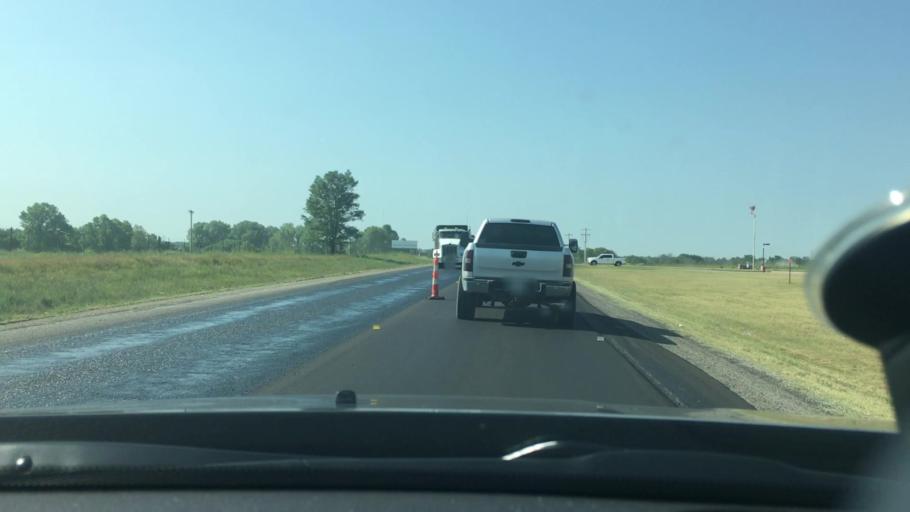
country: US
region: Oklahoma
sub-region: Garvin County
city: Lindsay
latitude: 34.7993
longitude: -97.5983
